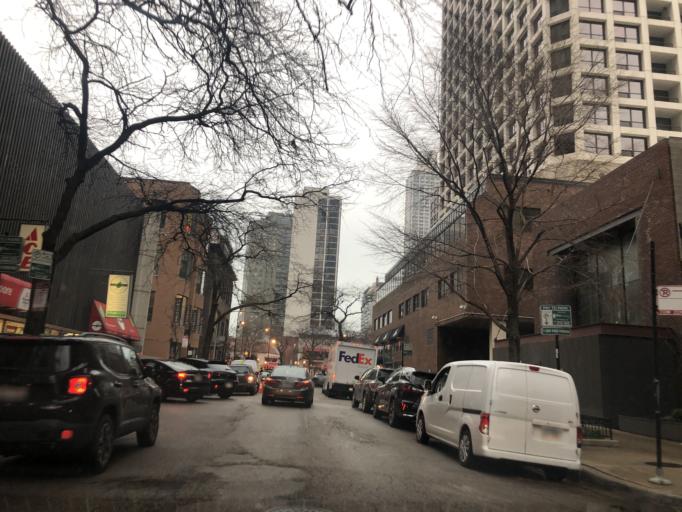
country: US
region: Illinois
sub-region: Cook County
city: Chicago
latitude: 41.9018
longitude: -87.6297
